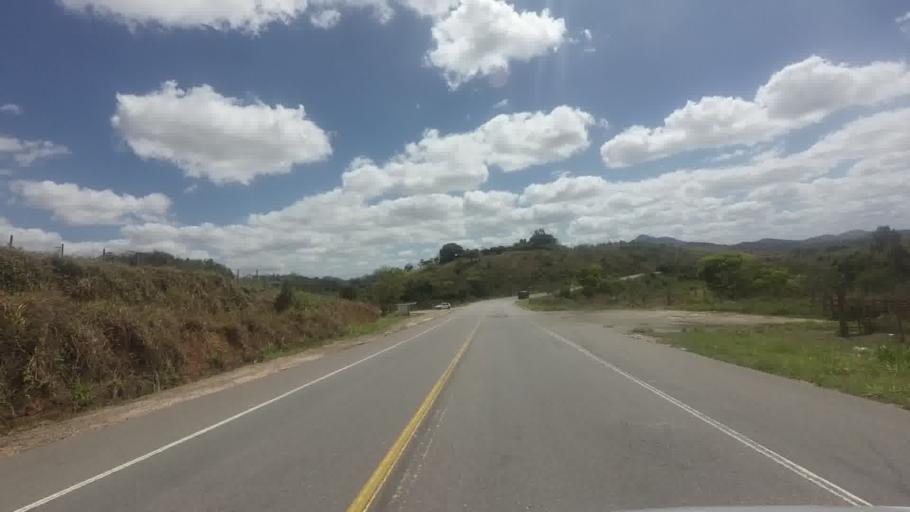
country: BR
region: Minas Gerais
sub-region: Recreio
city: Recreio
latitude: -21.6750
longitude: -42.3927
